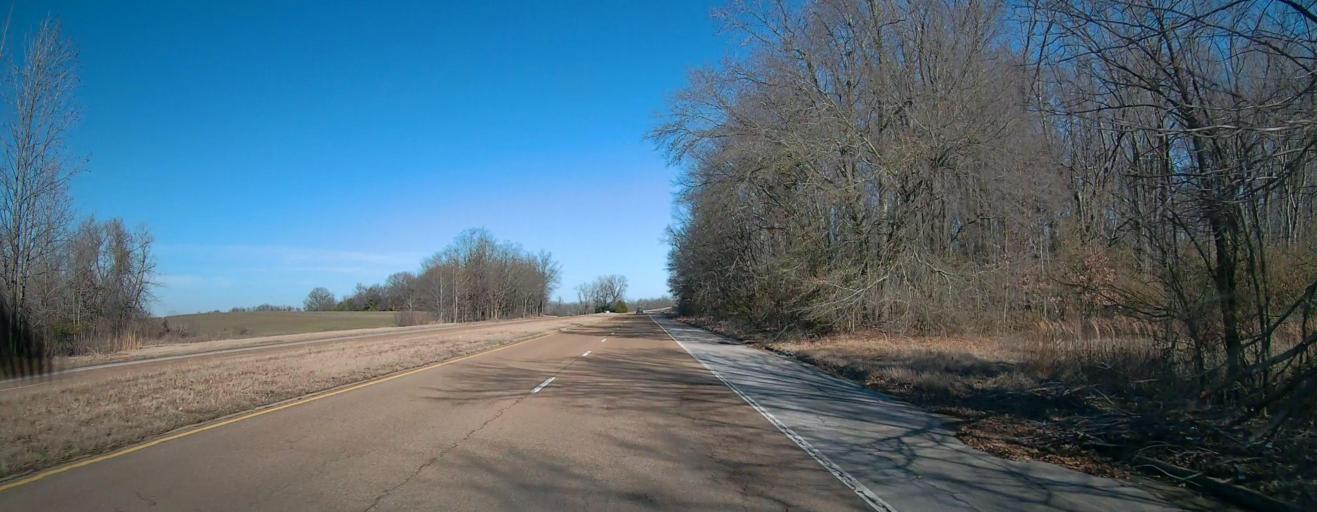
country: US
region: Tennessee
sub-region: Shelby County
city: Bartlett
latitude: 35.2559
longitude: -89.8923
